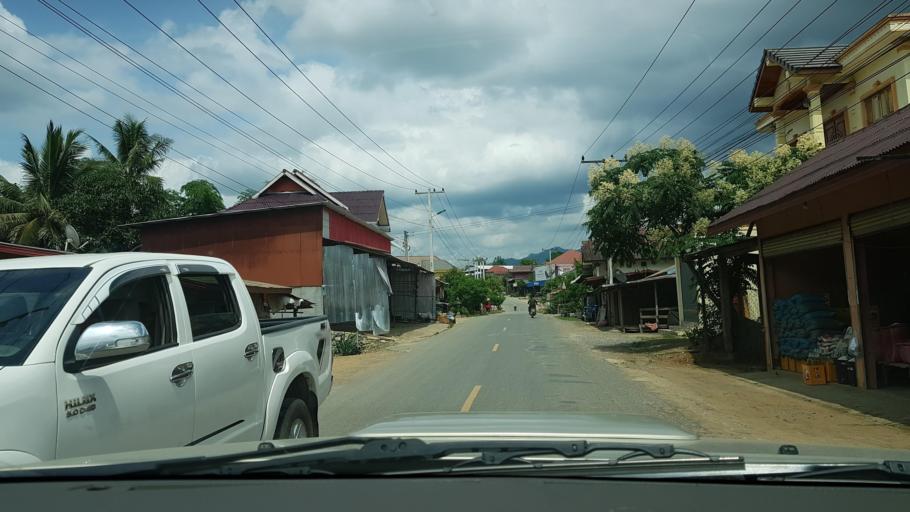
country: LA
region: Loungnamtha
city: Muang Nale
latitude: 20.1265
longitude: 101.4355
